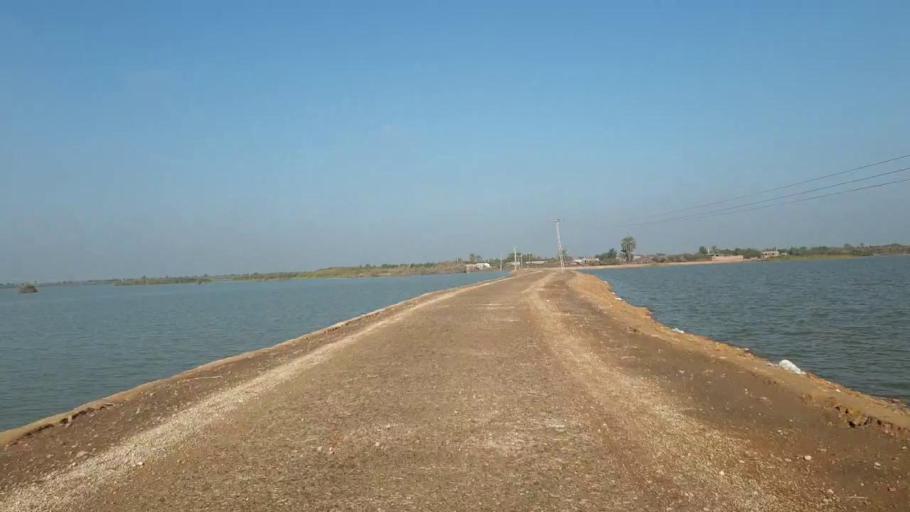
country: PK
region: Sindh
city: Shahdadpur
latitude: 25.8975
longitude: 68.5818
